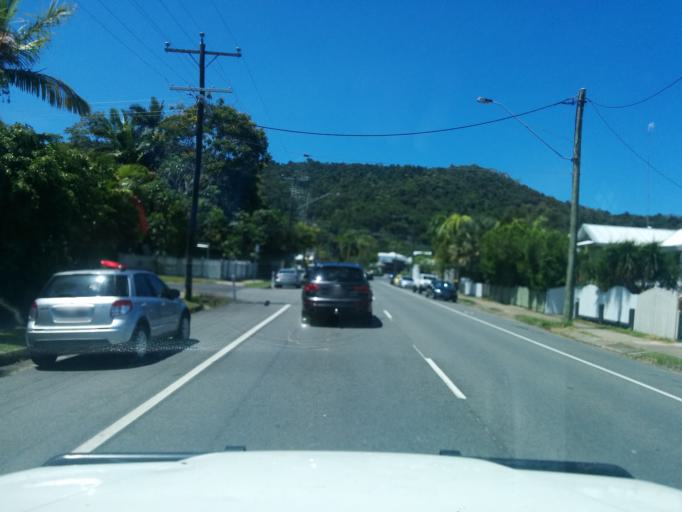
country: AU
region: Queensland
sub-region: Cairns
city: Cairns
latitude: -16.9025
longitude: 145.7420
